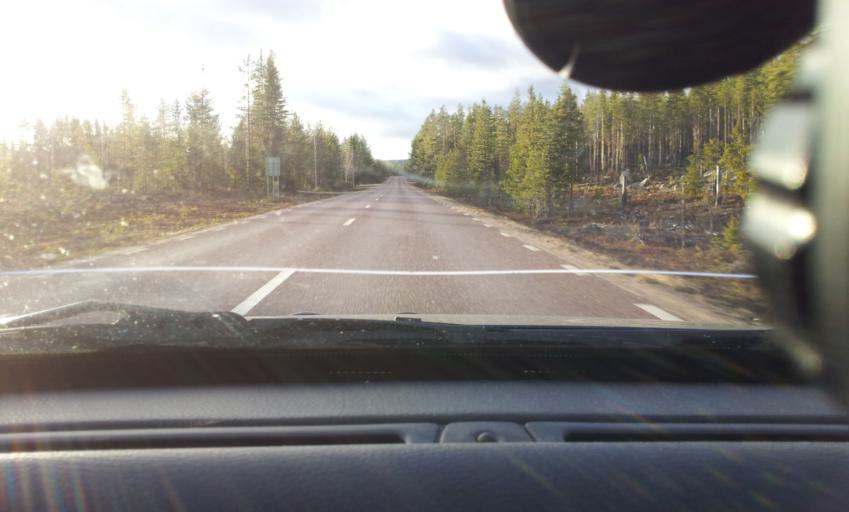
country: SE
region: Jaemtland
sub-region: Harjedalens Kommun
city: Sveg
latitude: 62.1843
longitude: 14.8721
